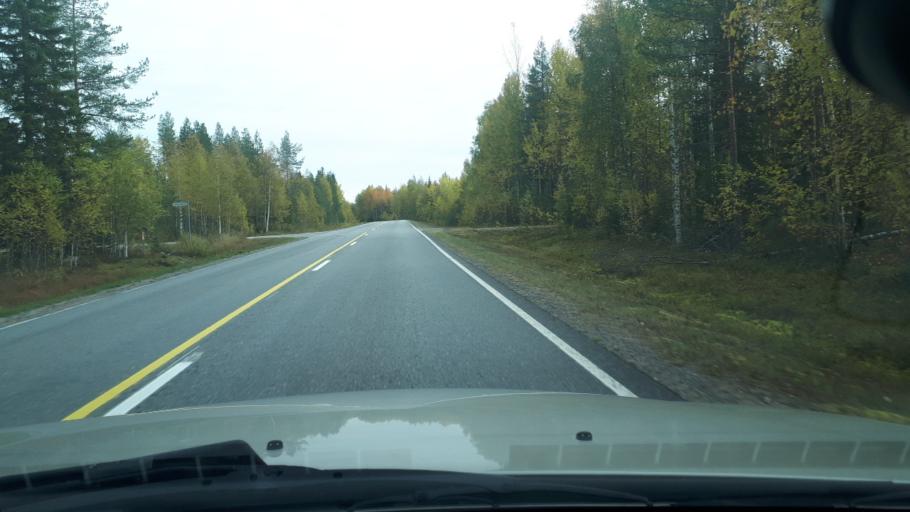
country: FI
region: Lapland
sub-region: Rovaniemi
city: Ranua
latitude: 66.0096
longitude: 26.2878
